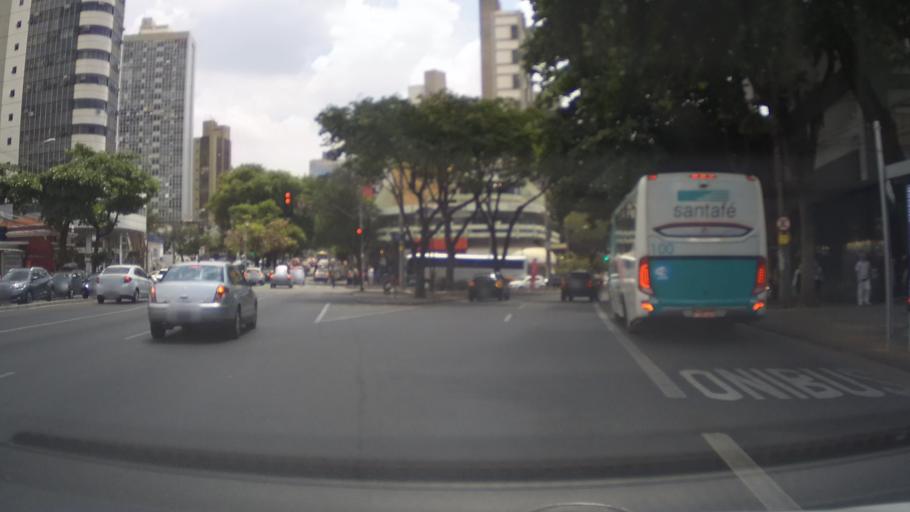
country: BR
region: Minas Gerais
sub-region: Belo Horizonte
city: Belo Horizonte
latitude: -19.9394
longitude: -43.9332
